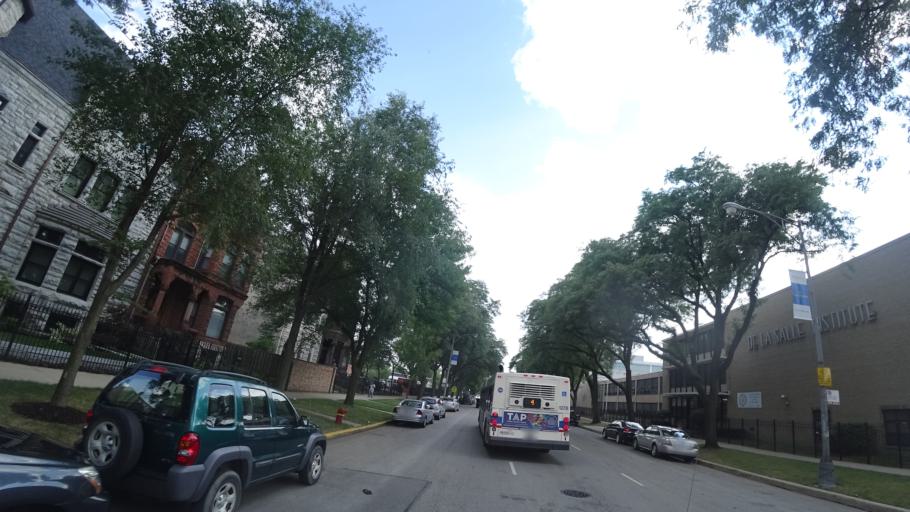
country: US
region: Illinois
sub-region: Cook County
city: Chicago
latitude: 41.8322
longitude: -87.6232
